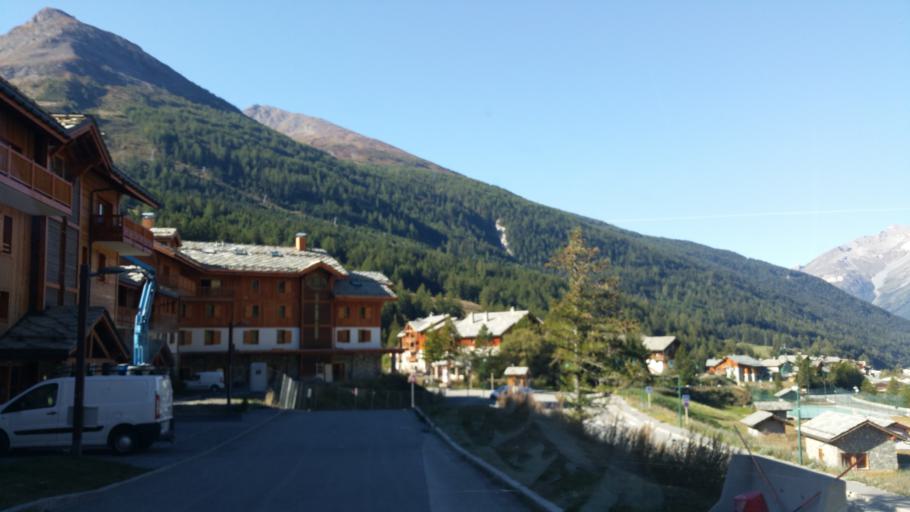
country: IT
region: Piedmont
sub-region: Provincia di Torino
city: Moncenisio
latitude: 45.2868
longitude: 6.9009
